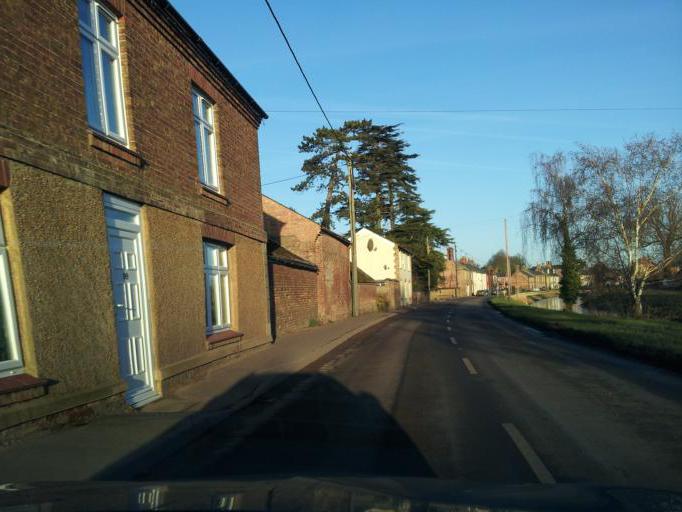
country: GB
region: England
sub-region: Norfolk
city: Outwell
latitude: 52.6006
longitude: 0.2141
